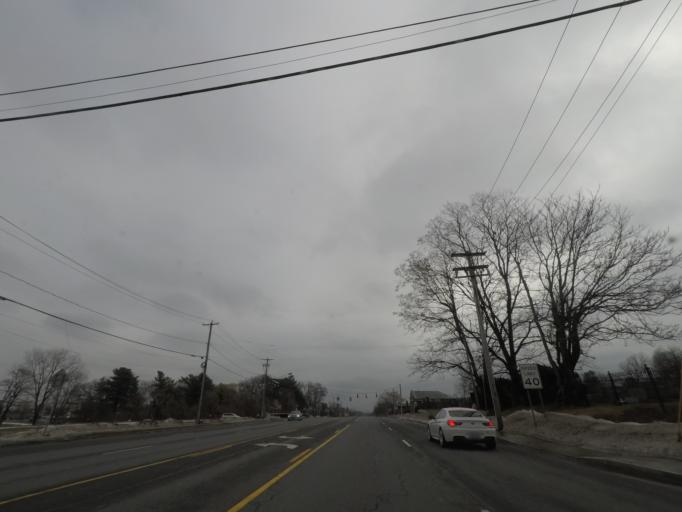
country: US
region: New York
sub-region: Albany County
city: McKownville
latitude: 42.6861
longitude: -73.8532
